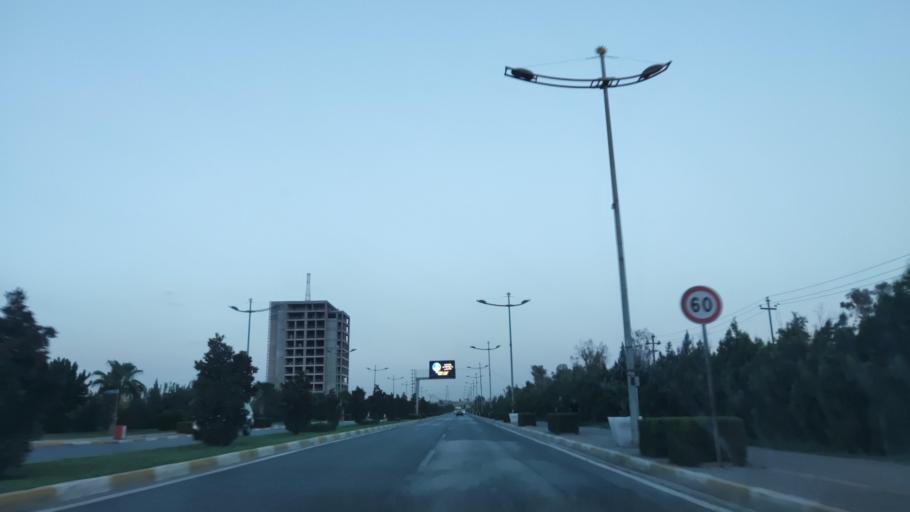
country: IQ
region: Arbil
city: Erbil
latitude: 36.1990
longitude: 43.9830
